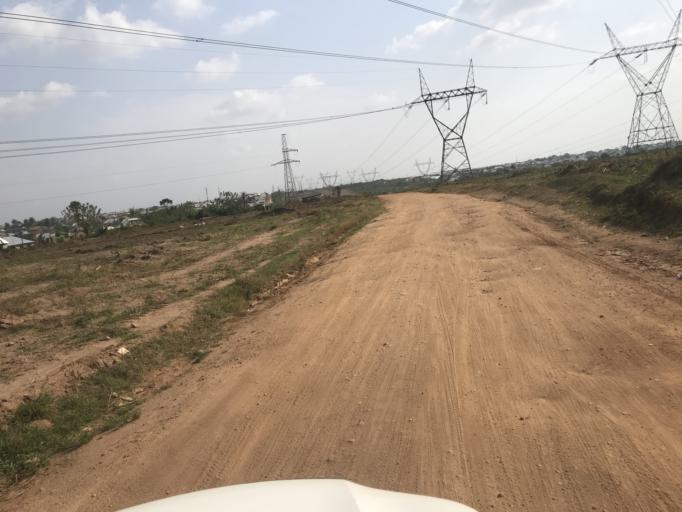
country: NG
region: Osun
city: Osogbo
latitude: 7.8323
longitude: 4.5713
